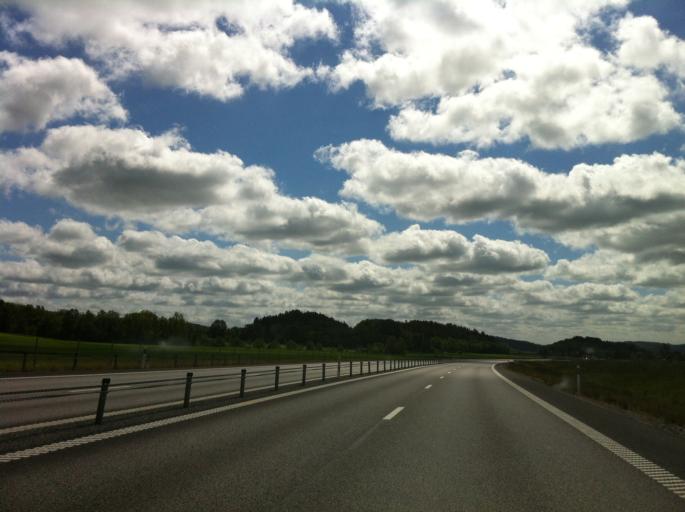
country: SE
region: Vaestra Goetaland
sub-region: Ale Kommun
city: Skepplanda
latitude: 58.0156
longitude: 12.1732
